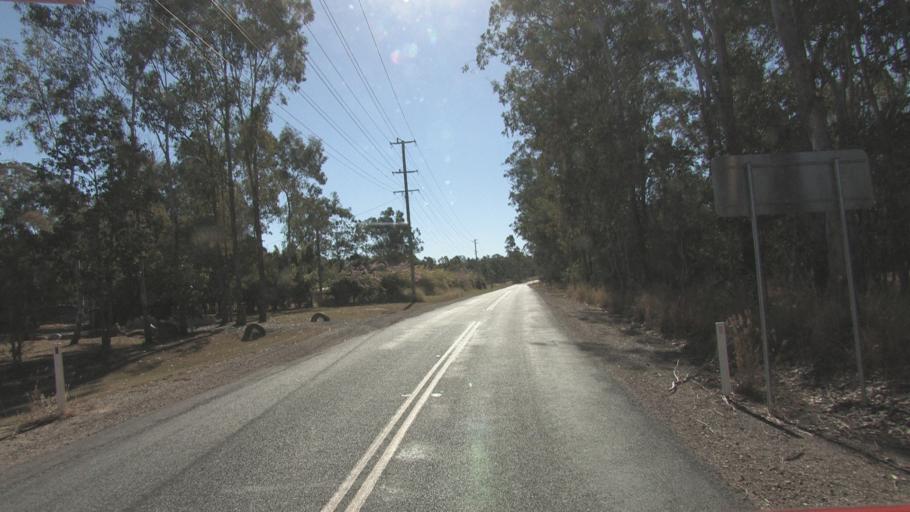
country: AU
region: Queensland
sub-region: Logan
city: North Maclean
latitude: -27.7645
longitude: 152.9977
